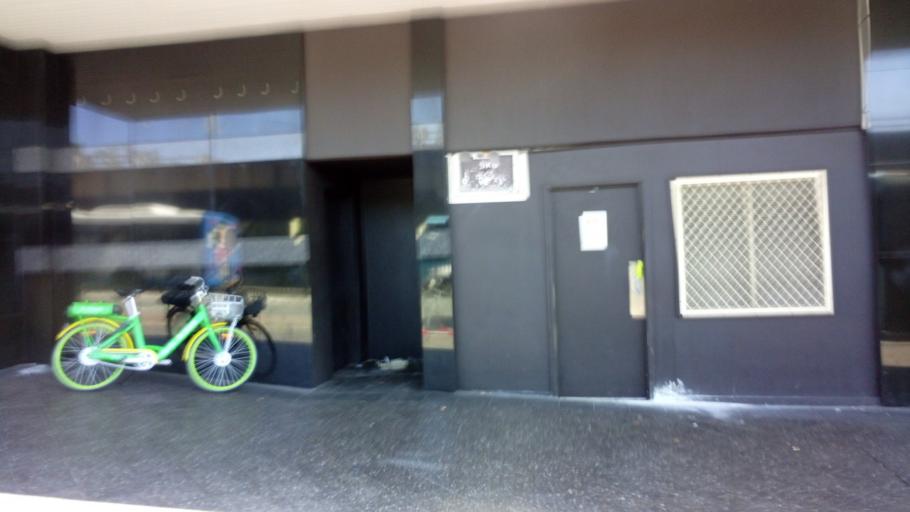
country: AU
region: New South Wales
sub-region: Waverley
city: Bondi Junction
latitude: -33.8910
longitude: 151.2485
